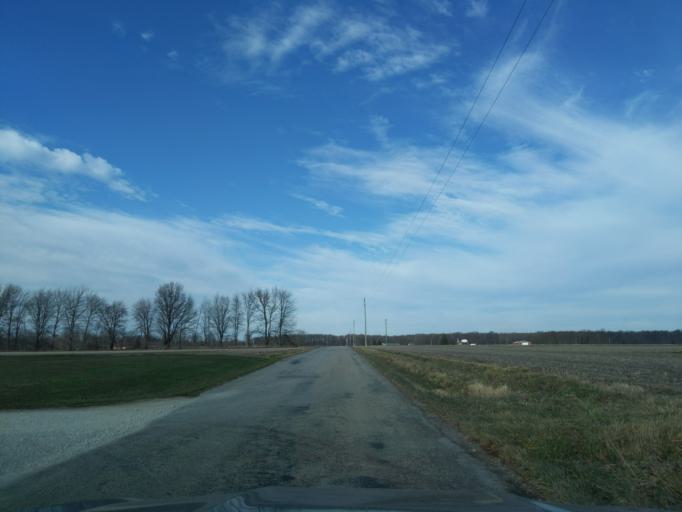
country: US
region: Indiana
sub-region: Decatur County
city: Greensburg
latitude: 39.2583
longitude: -85.4189
